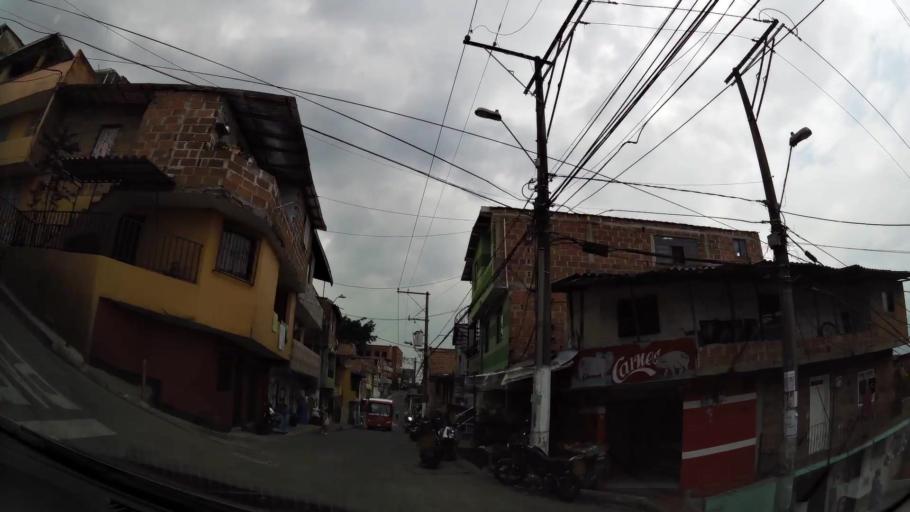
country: CO
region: Antioquia
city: Medellin
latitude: 6.2895
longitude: -75.5469
